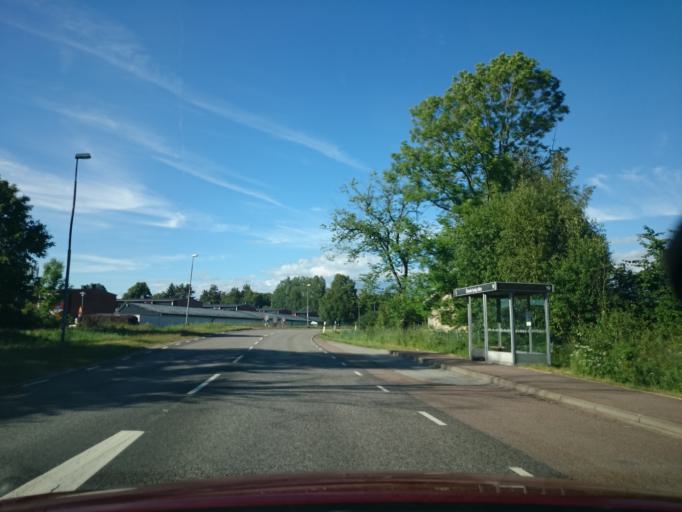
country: SE
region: Vaestra Goetaland
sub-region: Lerums Kommun
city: Stenkullen
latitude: 57.7880
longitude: 12.3087
